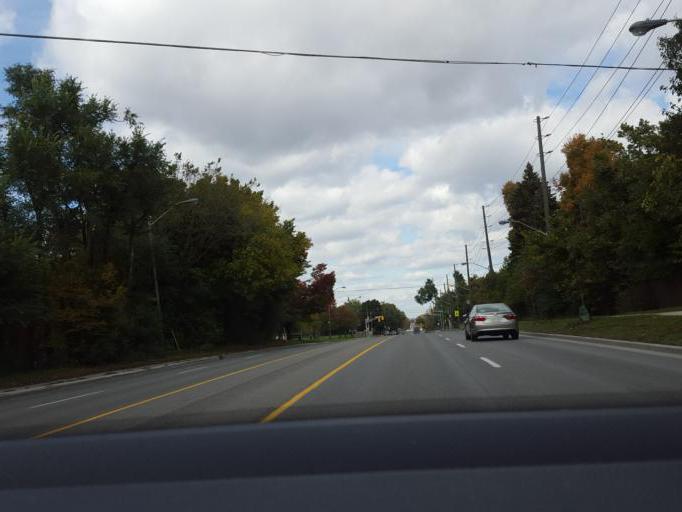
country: CA
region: Ontario
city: Willowdale
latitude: 43.7390
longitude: -79.3569
